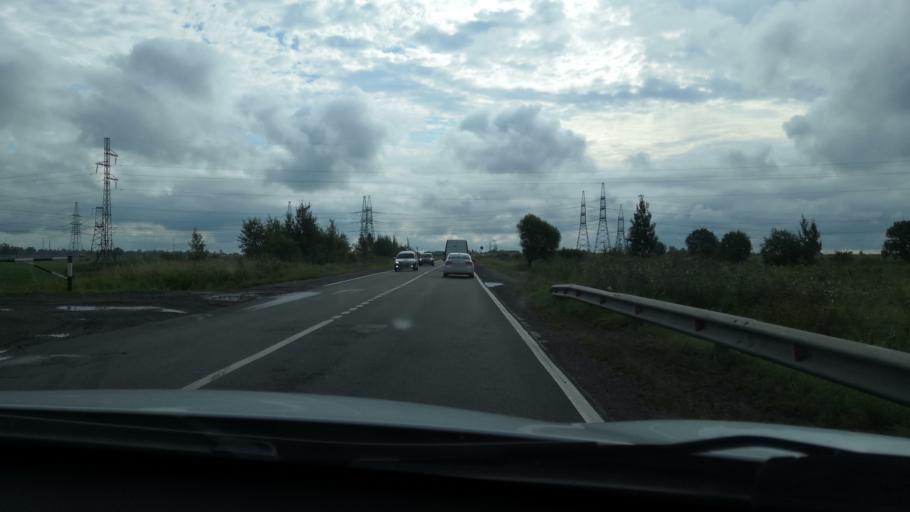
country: RU
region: Leningrad
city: Fedorovskoye
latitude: 59.7076
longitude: 30.5286
